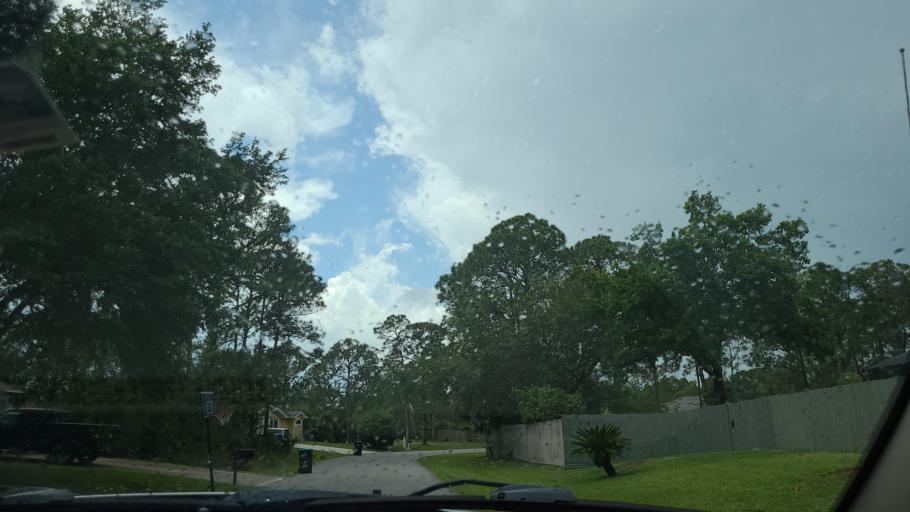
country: US
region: Florida
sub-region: Brevard County
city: Grant-Valkaria
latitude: 27.9485
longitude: -80.6360
